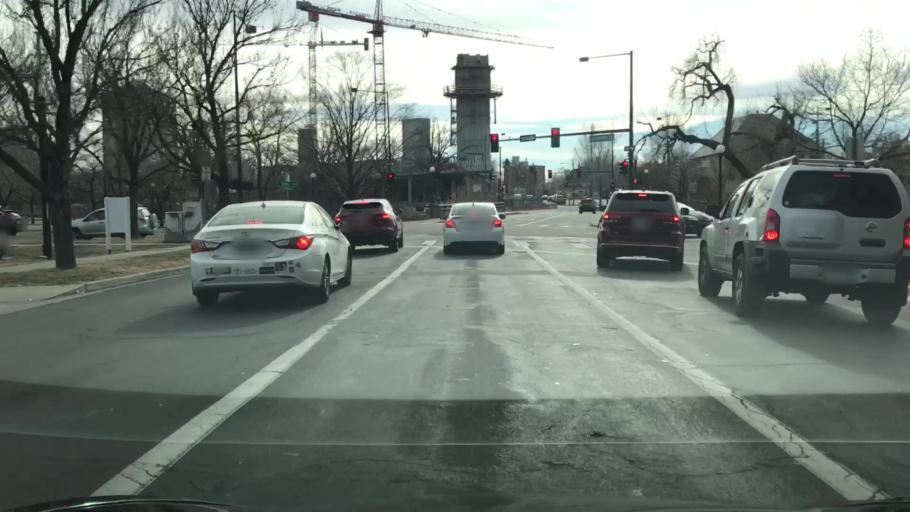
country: US
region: Colorado
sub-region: Denver County
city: Denver
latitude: 39.7246
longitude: -104.9837
